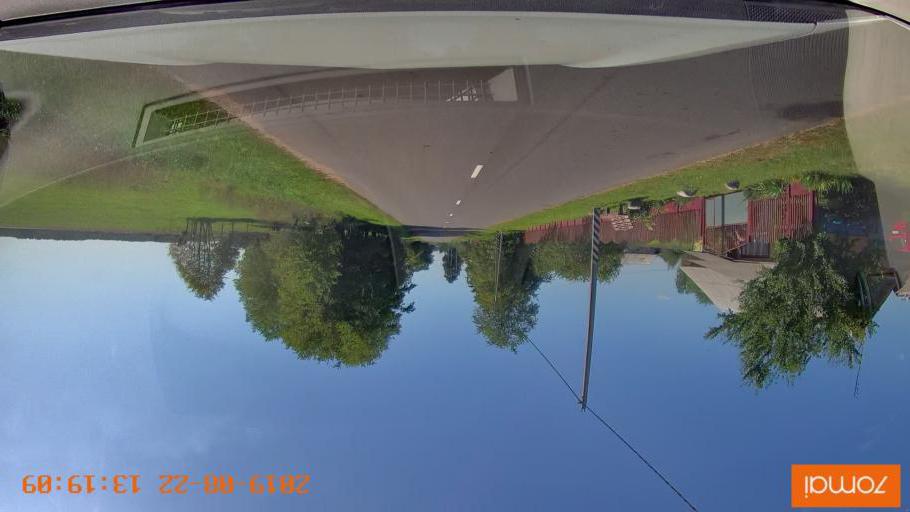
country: BY
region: Minsk
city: Urechcha
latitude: 53.2363
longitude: 27.9478
